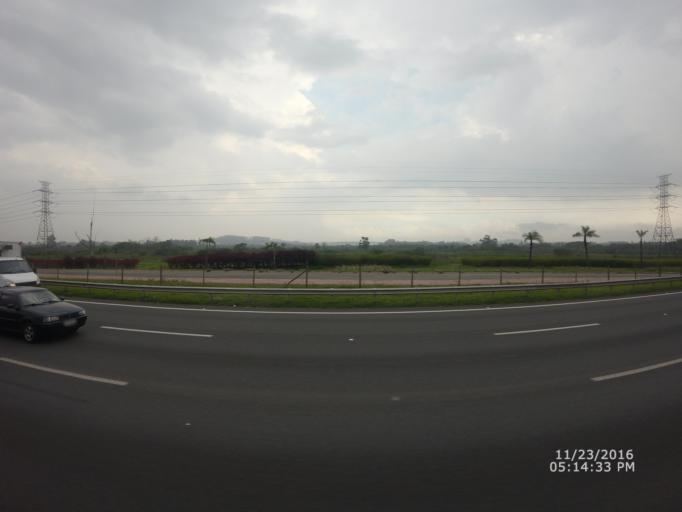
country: BR
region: Sao Paulo
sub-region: Guarulhos
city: Guarulhos
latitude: -23.4746
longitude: -46.5125
